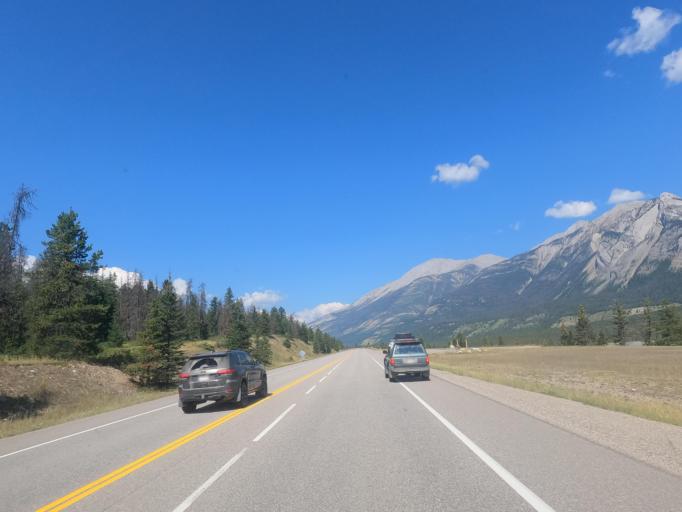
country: CA
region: Alberta
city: Jasper Park Lodge
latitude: 52.9421
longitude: -118.0394
